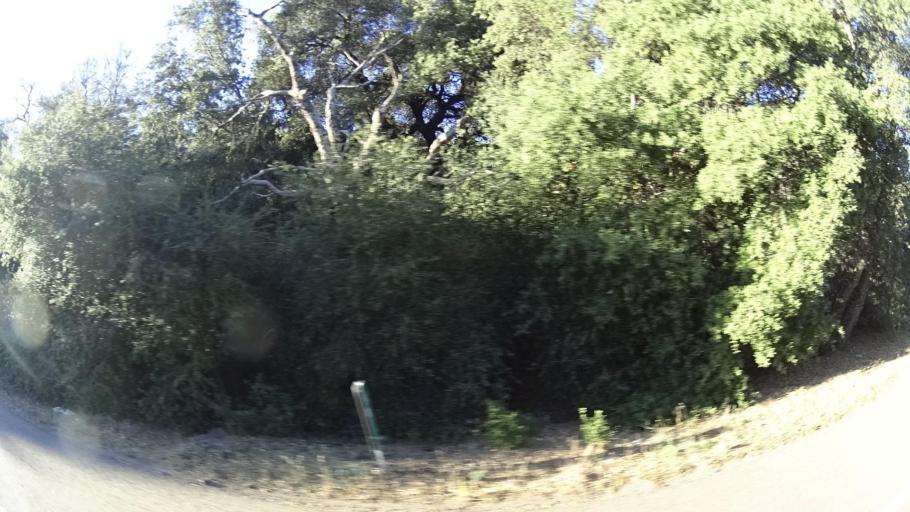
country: US
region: California
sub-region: San Diego County
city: Descanso
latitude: 32.8555
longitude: -116.5790
